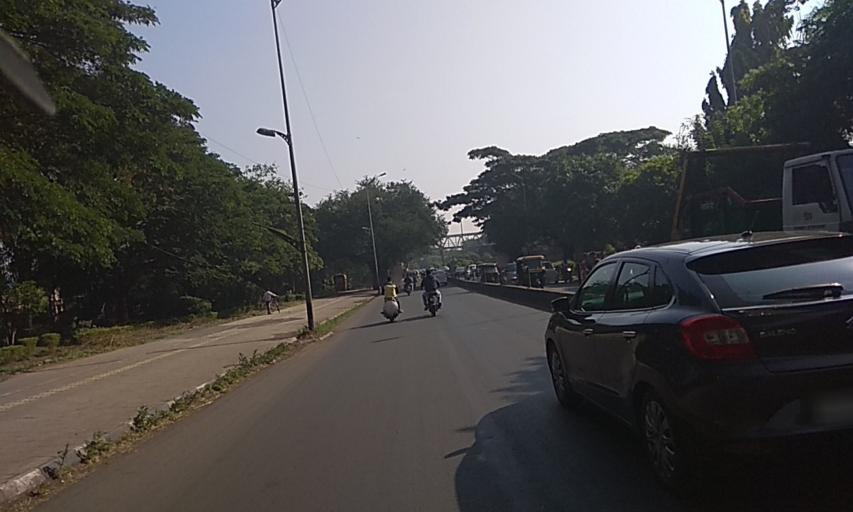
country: IN
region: Maharashtra
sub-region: Pune Division
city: Pune
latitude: 18.5067
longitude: 73.8955
